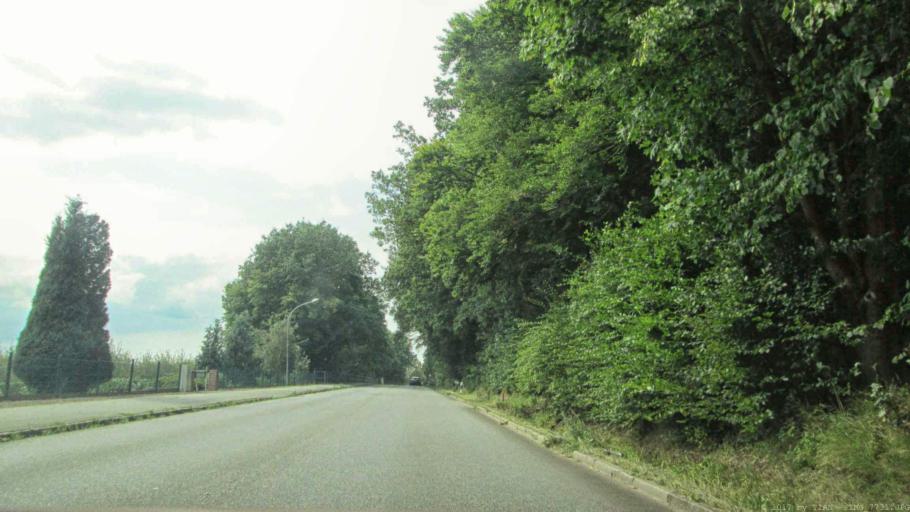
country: DE
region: Schleswig-Holstein
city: Escheburg
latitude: 53.4610
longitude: 10.3253
